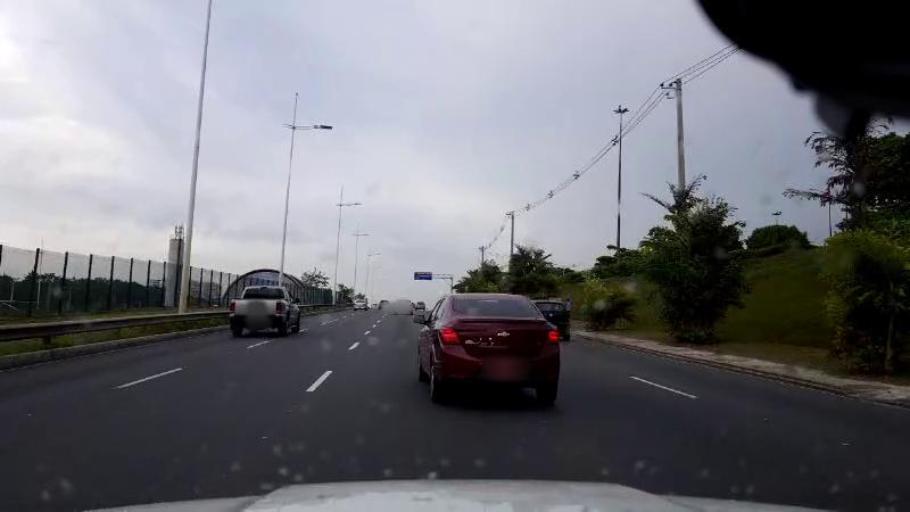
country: BR
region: Bahia
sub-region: Salvador
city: Salvador
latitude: -12.9536
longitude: -38.4278
